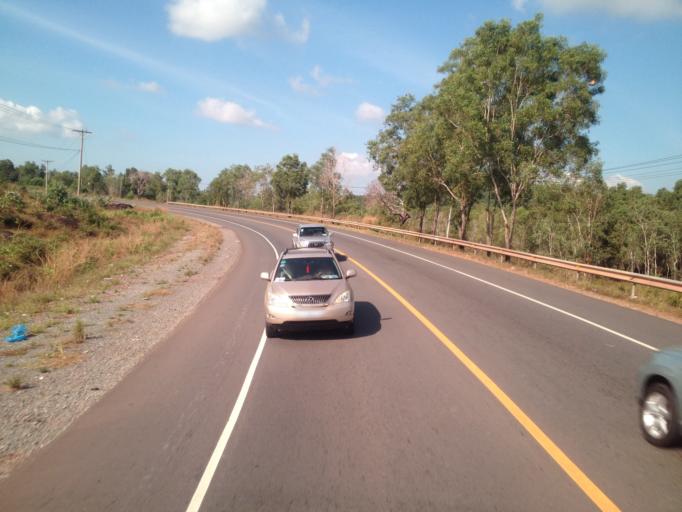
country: KH
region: Preah Sihanouk
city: Sihanoukville
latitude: 10.6067
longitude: 103.6146
